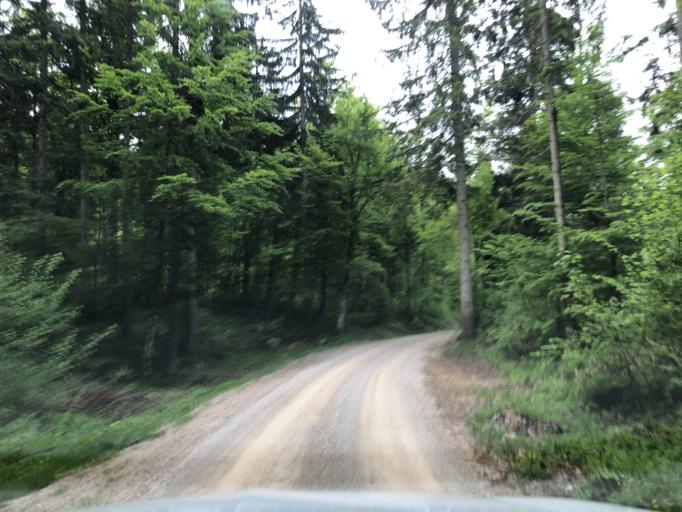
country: SI
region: Bloke
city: Nova Vas
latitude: 45.7492
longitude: 14.4658
